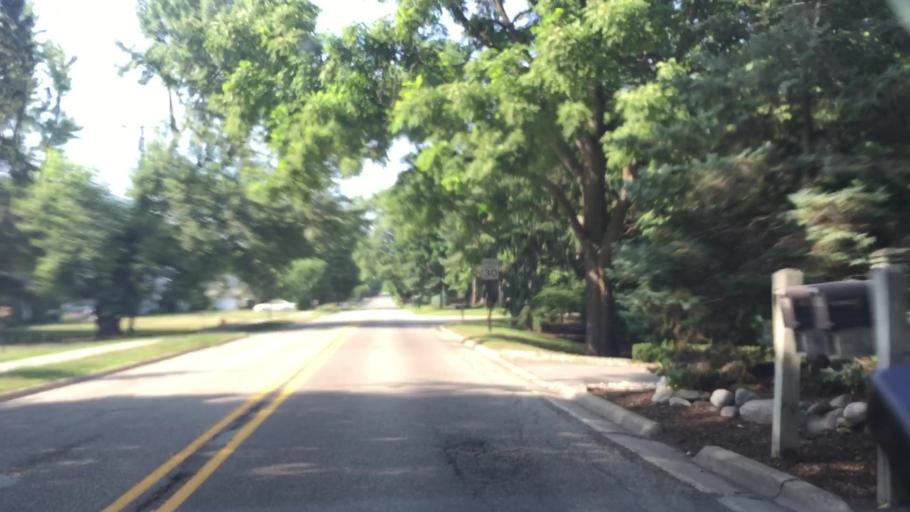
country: US
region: Michigan
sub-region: Oakland County
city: Franklin
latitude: 42.5383
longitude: -83.2966
